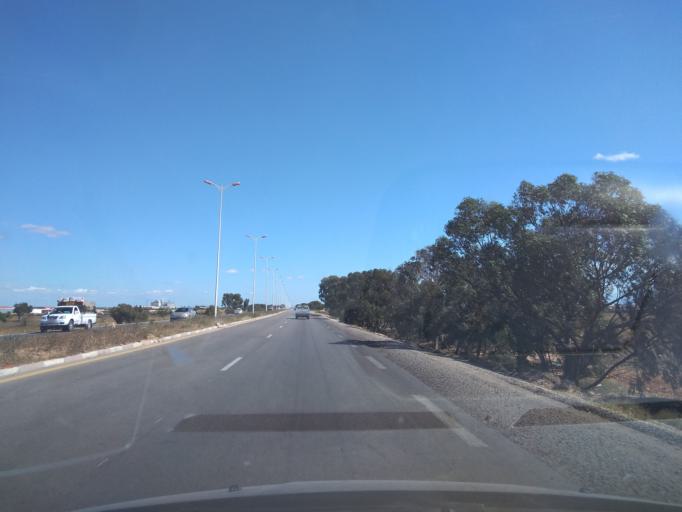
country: TN
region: Safaqis
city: Al Qarmadah
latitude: 34.8474
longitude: 10.7481
